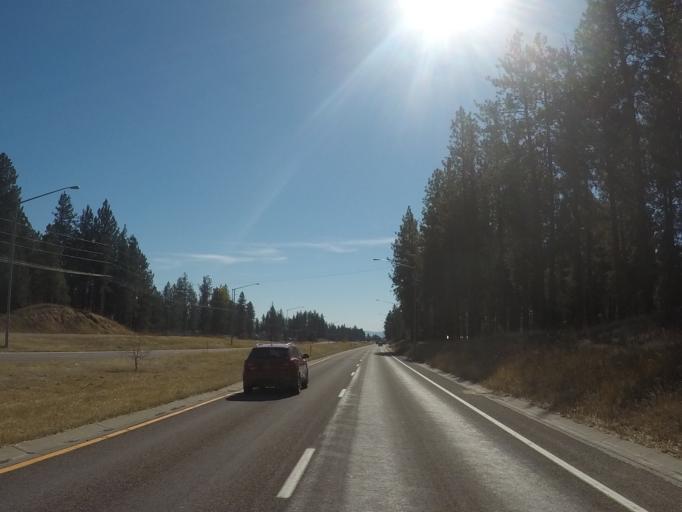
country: US
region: Montana
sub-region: Lake County
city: Pablo
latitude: 47.6107
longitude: -114.1133
